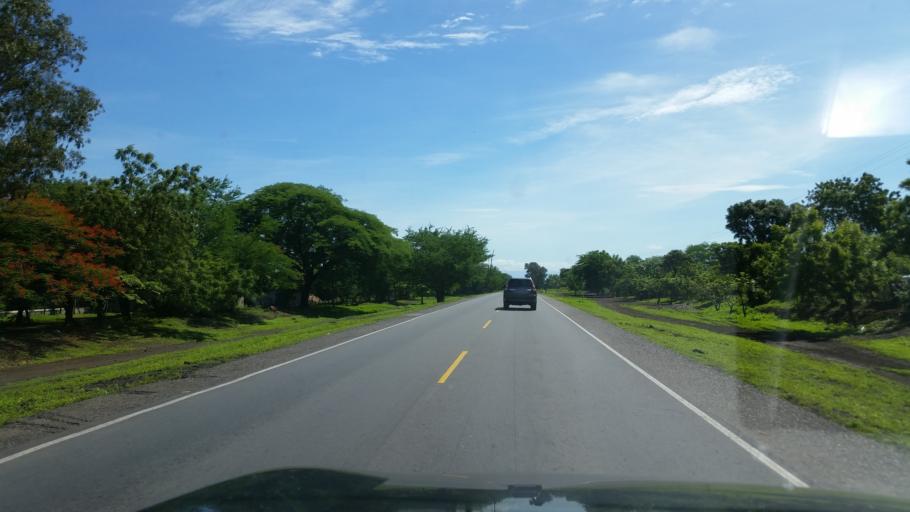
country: NI
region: Chinandega
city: El Viejo
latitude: 12.7511
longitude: -87.0676
